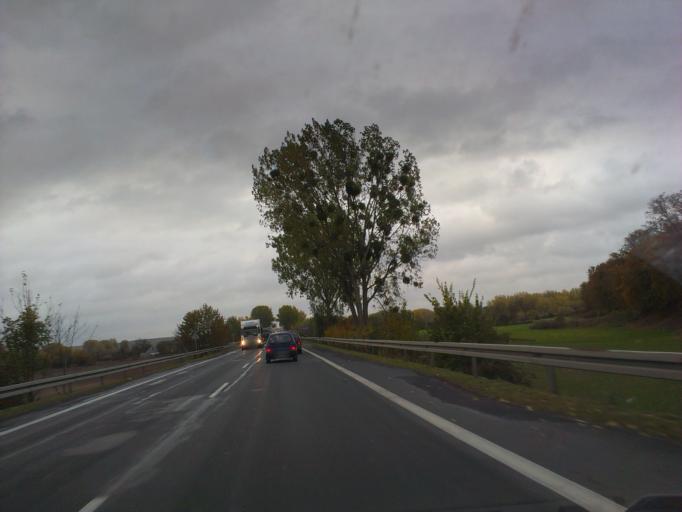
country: PL
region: Kujawsko-Pomorskie
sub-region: Powiat chelminski
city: Chelmno
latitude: 53.3803
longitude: 18.4169
